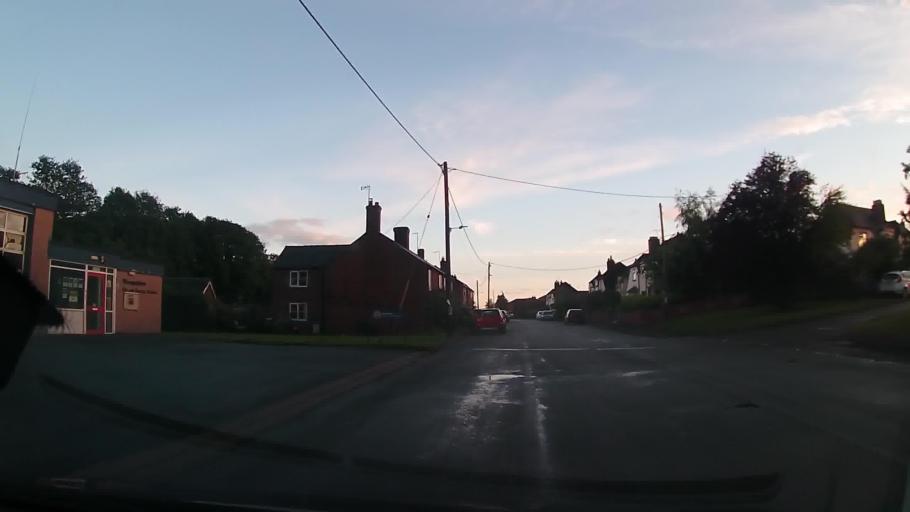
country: GB
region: England
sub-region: Shropshire
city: Prees
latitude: 52.8978
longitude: -2.6695
